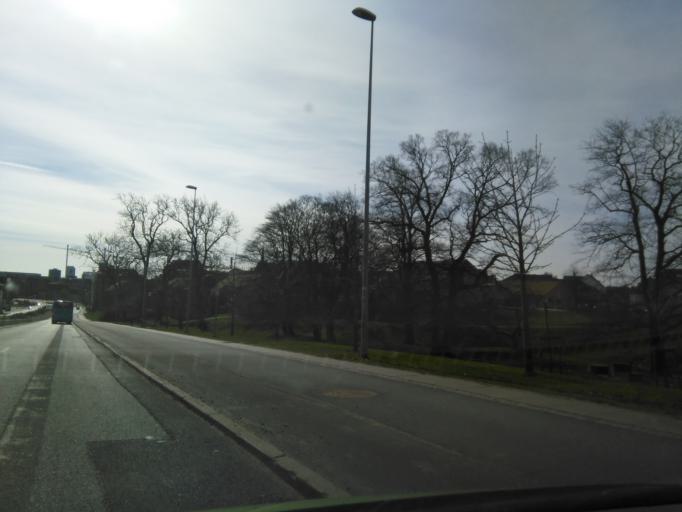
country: DK
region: Central Jutland
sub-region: Arhus Kommune
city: Arhus
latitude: 56.1652
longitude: 10.2088
